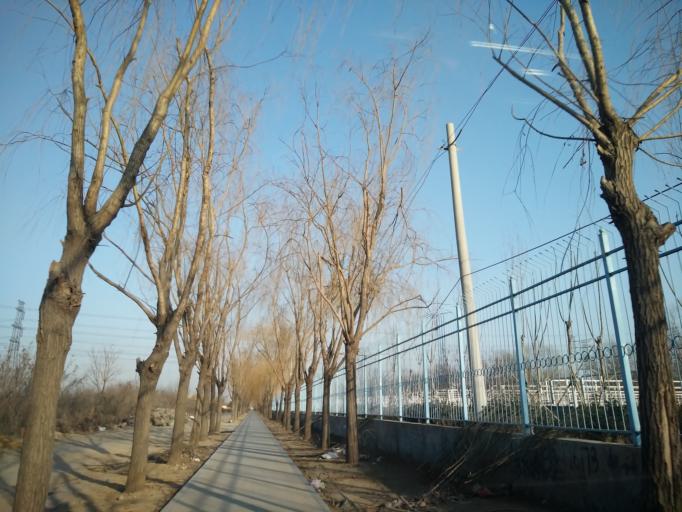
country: CN
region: Beijing
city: Xingfeng
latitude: 39.7213
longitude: 116.3796
